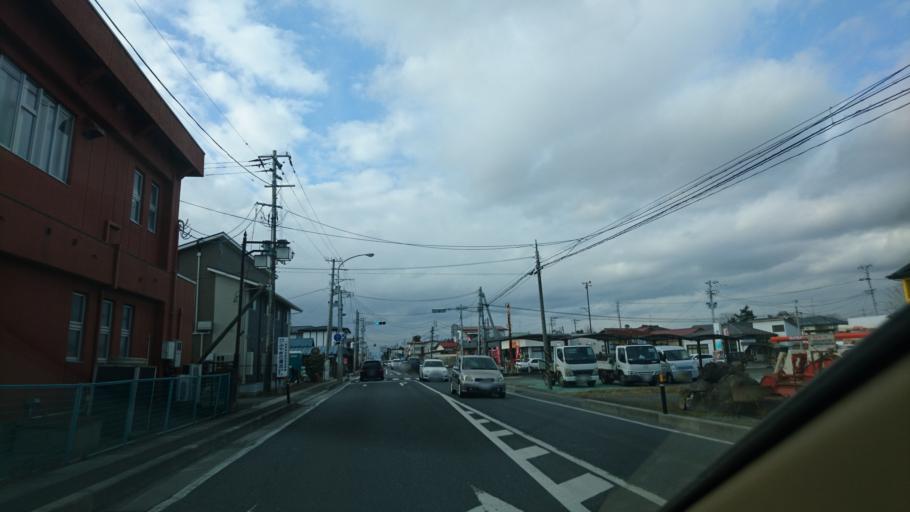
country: JP
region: Miyagi
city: Kogota
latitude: 38.5602
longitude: 141.0247
